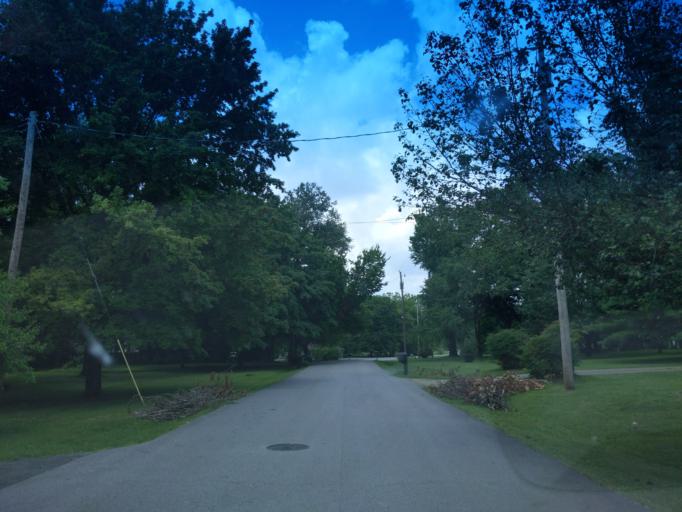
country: US
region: Tennessee
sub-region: Williamson County
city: Brentwood Estates
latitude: 36.0272
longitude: -86.7782
